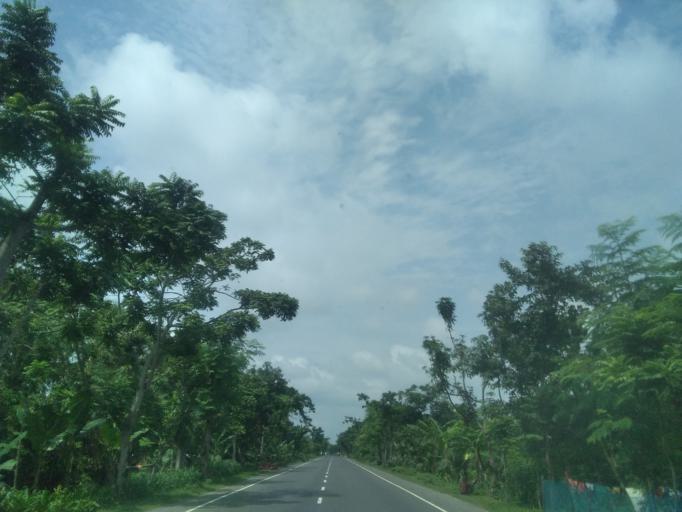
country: BD
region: Khulna
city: Kesabpur
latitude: 22.8040
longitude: 89.2354
